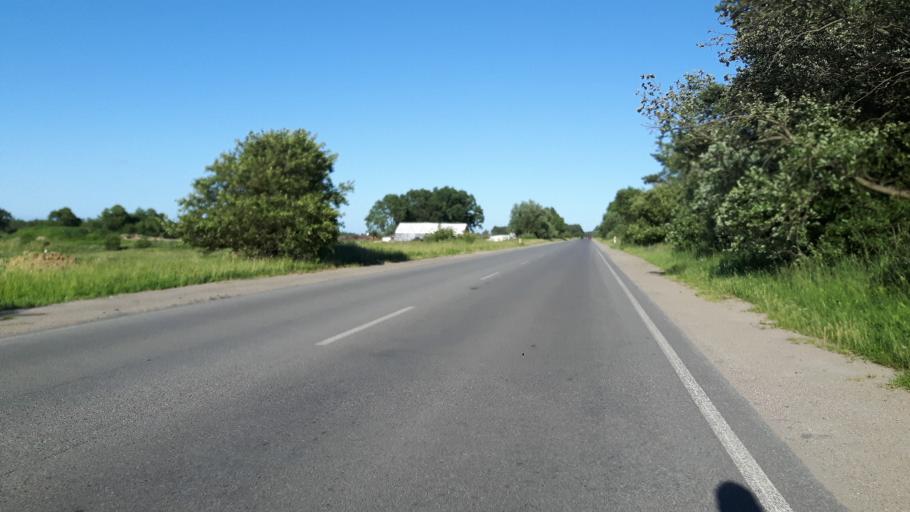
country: PL
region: Pomeranian Voivodeship
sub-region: Powiat pucki
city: Mrzezino
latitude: 54.6050
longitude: 18.4353
